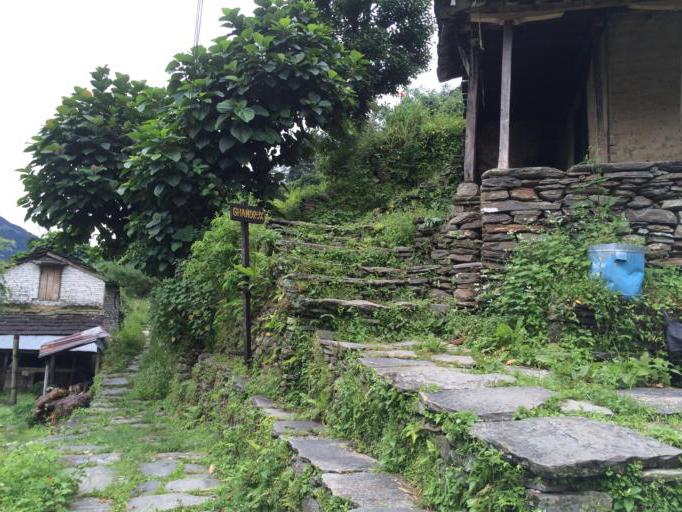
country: NP
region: Western Region
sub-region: Dhawalagiri Zone
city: Chitre
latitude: 28.3713
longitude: 83.8157
